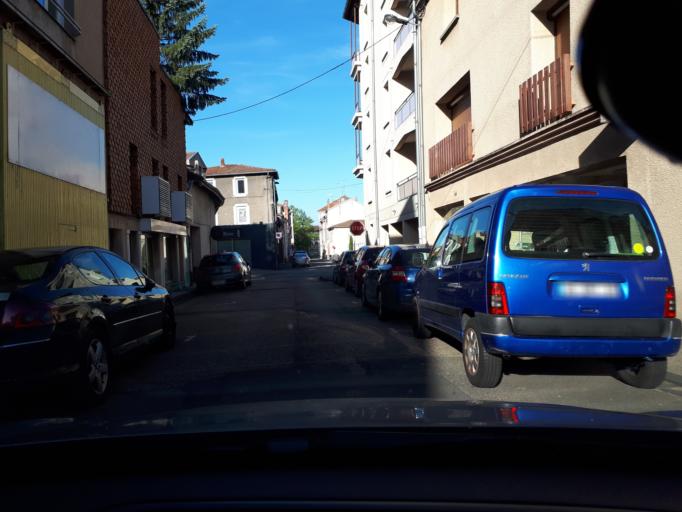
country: FR
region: Rhone-Alpes
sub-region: Departement de la Loire
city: Feurs
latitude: 45.7448
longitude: 4.2233
